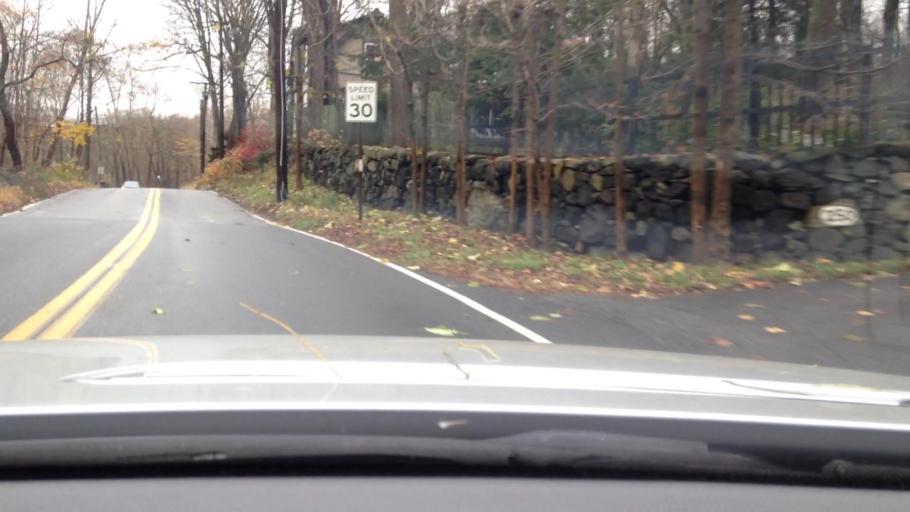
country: US
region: New York
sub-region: Westchester County
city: Croton-on-Hudson
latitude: 41.2337
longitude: -73.8875
